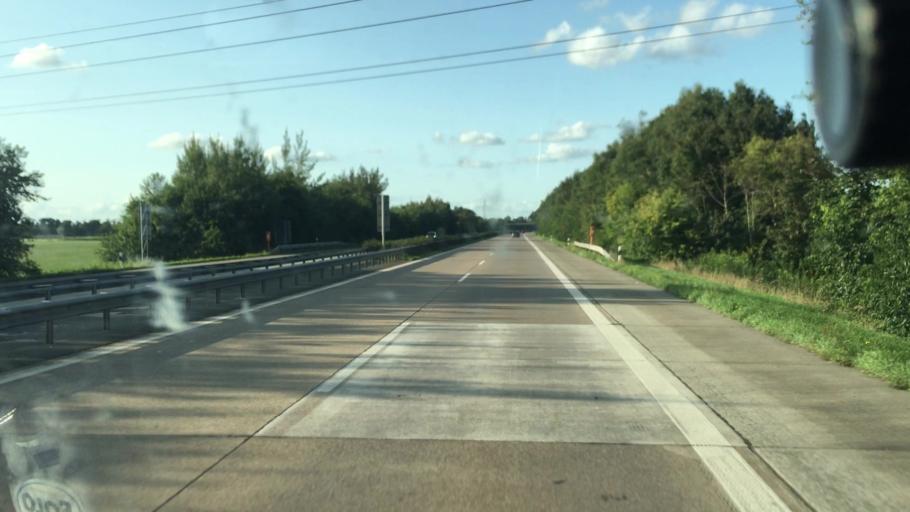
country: DE
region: Lower Saxony
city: Wiefelstede
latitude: 53.3123
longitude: 8.1427
